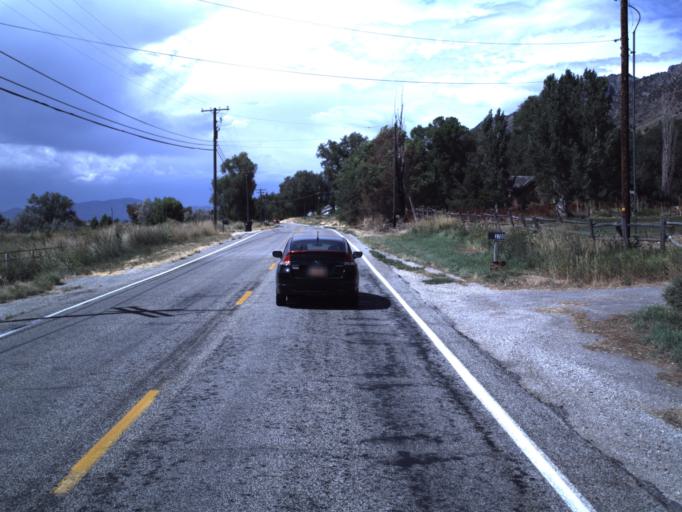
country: US
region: Utah
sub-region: Box Elder County
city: Brigham City
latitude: 41.5755
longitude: -112.0318
